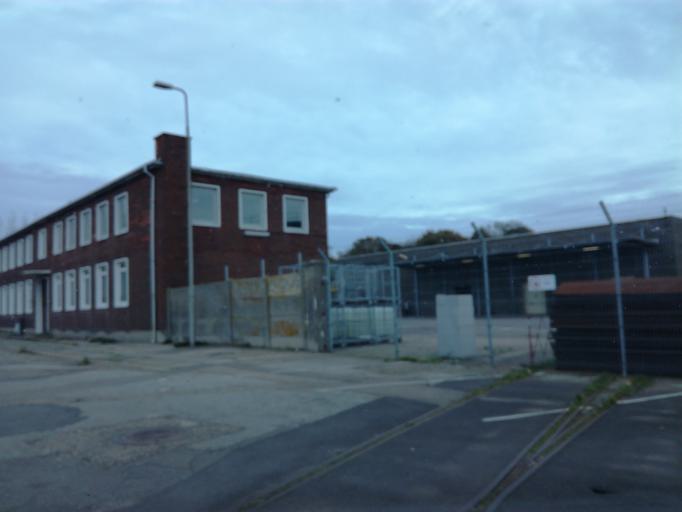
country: DK
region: South Denmark
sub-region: Fredericia Kommune
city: Fredericia
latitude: 55.5579
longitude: 9.7631
